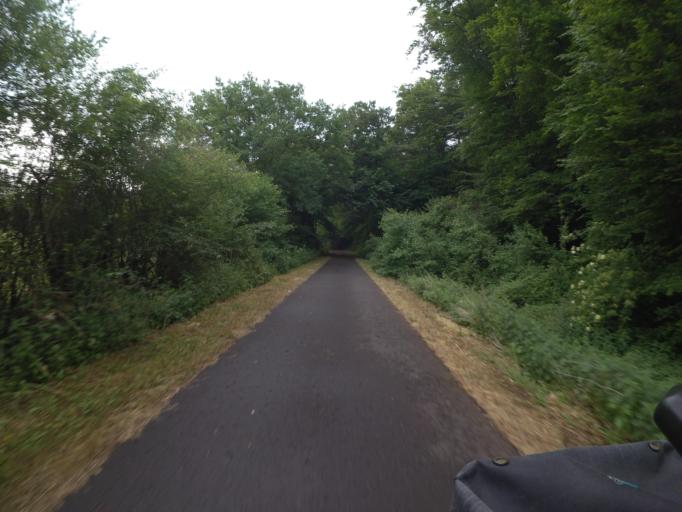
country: DE
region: Rheinland-Pfalz
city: Osann-Monzel
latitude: 49.9364
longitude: 6.9519
